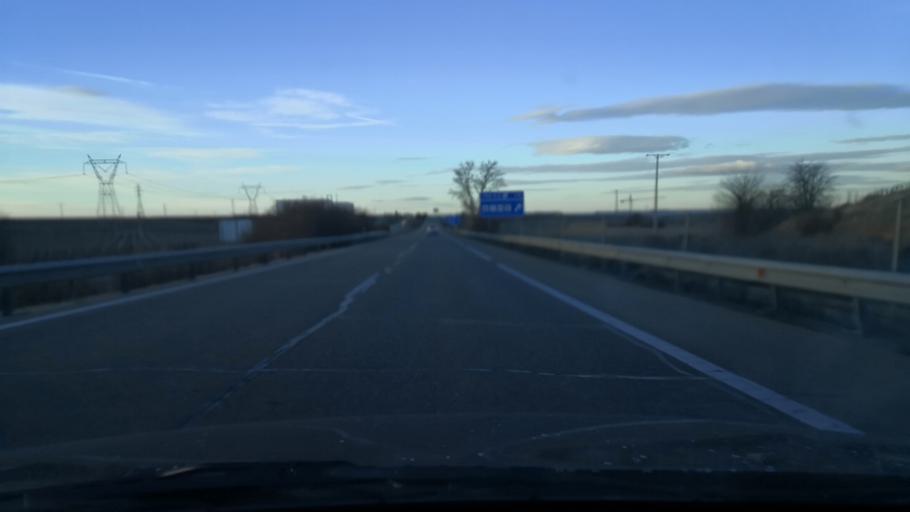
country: ES
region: Castille and Leon
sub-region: Provincia de Valladolid
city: Rueda
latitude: 41.4333
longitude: -4.9724
